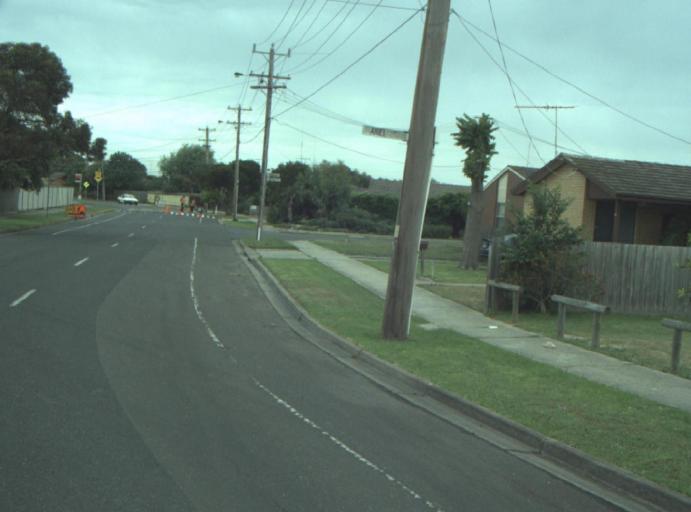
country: AU
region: Victoria
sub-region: Greater Geelong
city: Breakwater
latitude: -38.1760
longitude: 144.3921
